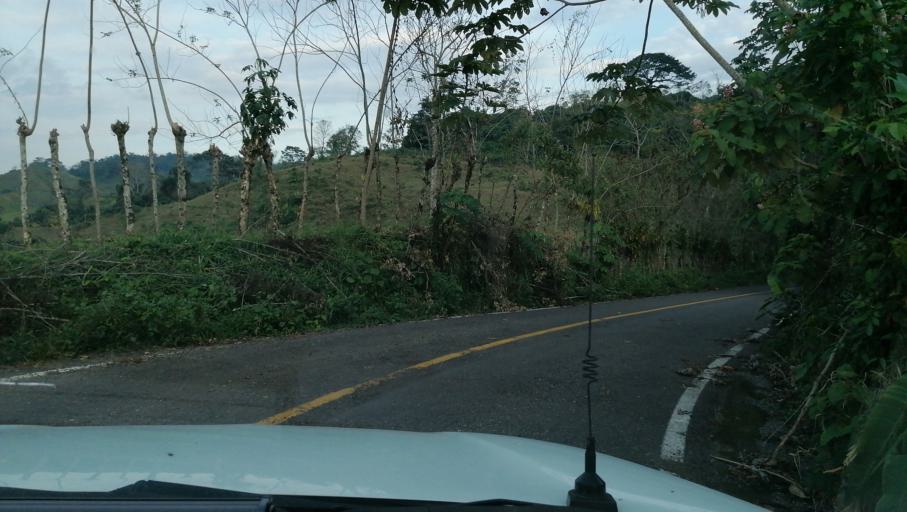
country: MX
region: Chiapas
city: Pichucalco
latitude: 17.5145
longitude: -93.2060
